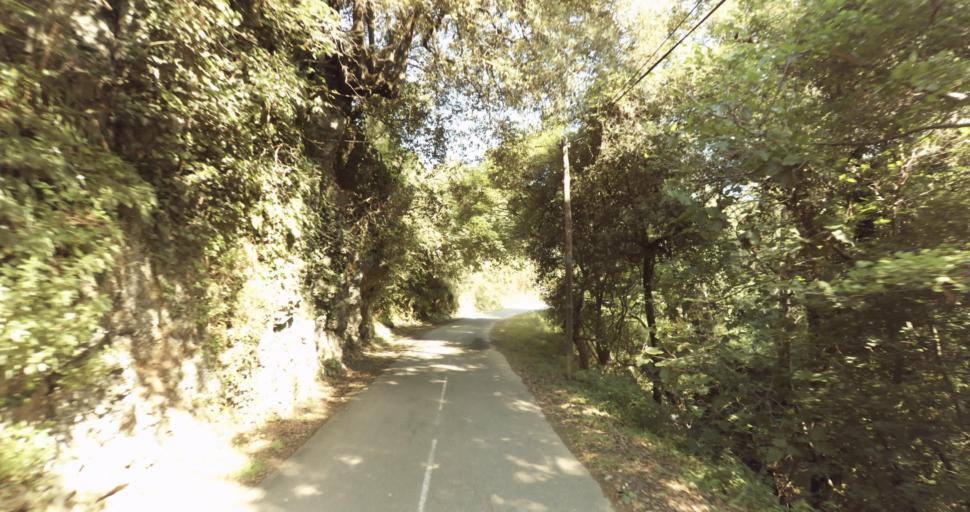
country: FR
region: Corsica
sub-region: Departement de la Haute-Corse
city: Biguglia
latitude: 42.6320
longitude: 9.4156
